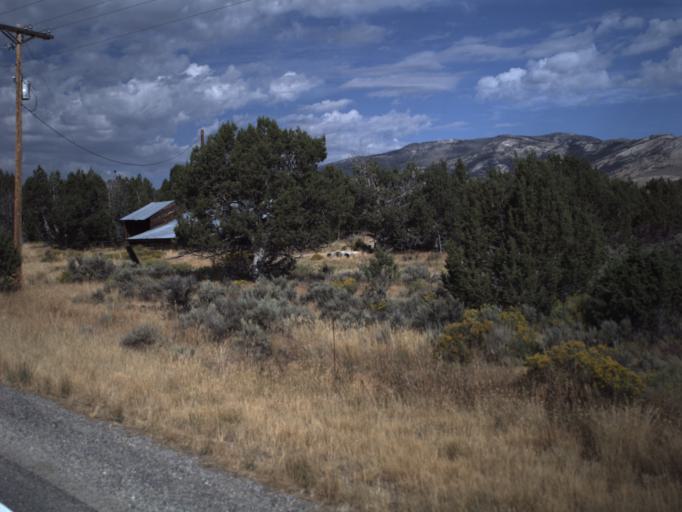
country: US
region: Idaho
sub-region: Cassia County
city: Burley
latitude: 41.8196
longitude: -113.4056
